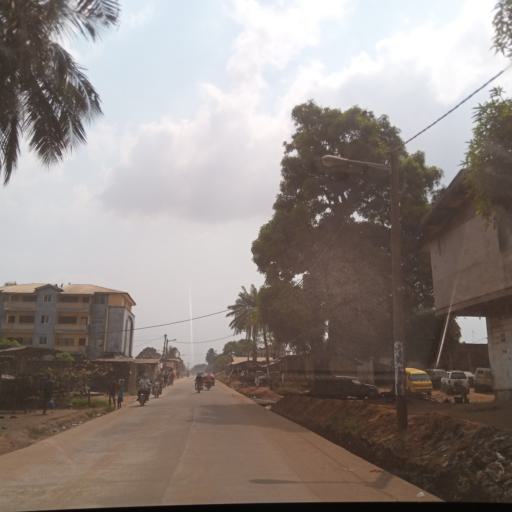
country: LR
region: Montserrado
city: Monrovia
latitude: 6.2884
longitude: -10.6898
